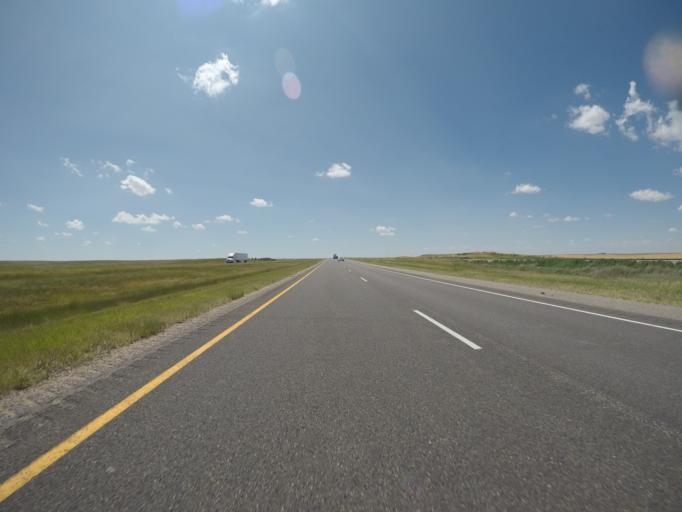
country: US
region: Colorado
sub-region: Lincoln County
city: Hugo
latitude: 39.2859
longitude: -103.1935
